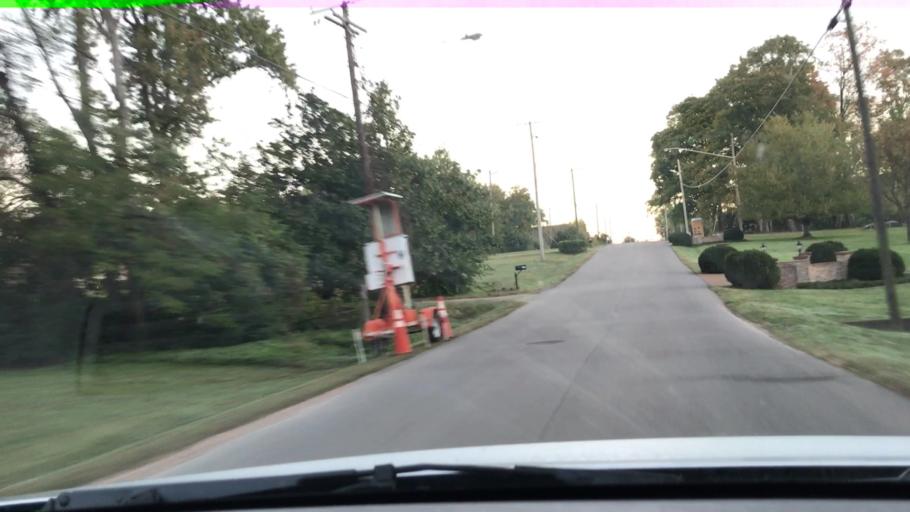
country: US
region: Tennessee
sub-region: Williamson County
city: Brentwood
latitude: 36.0376
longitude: -86.7715
